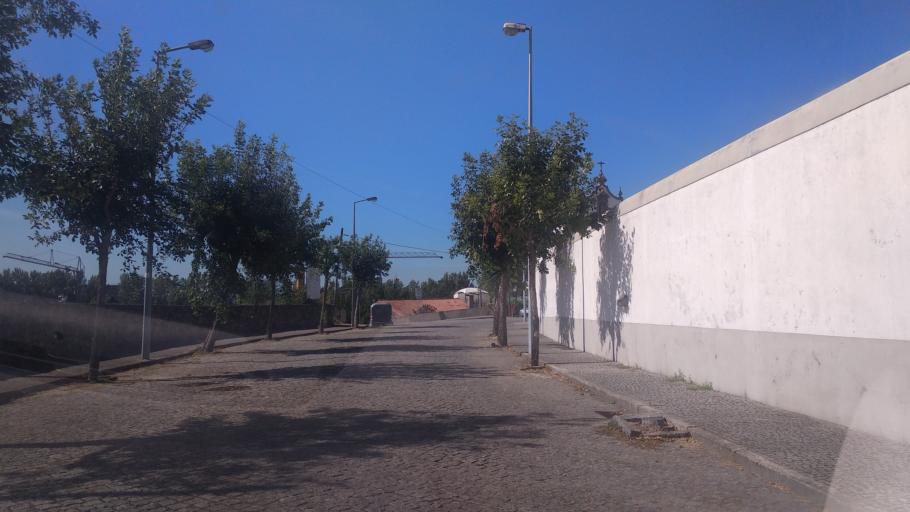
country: PT
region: Braga
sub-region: Braga
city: Braga
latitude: 41.5591
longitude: -8.4389
